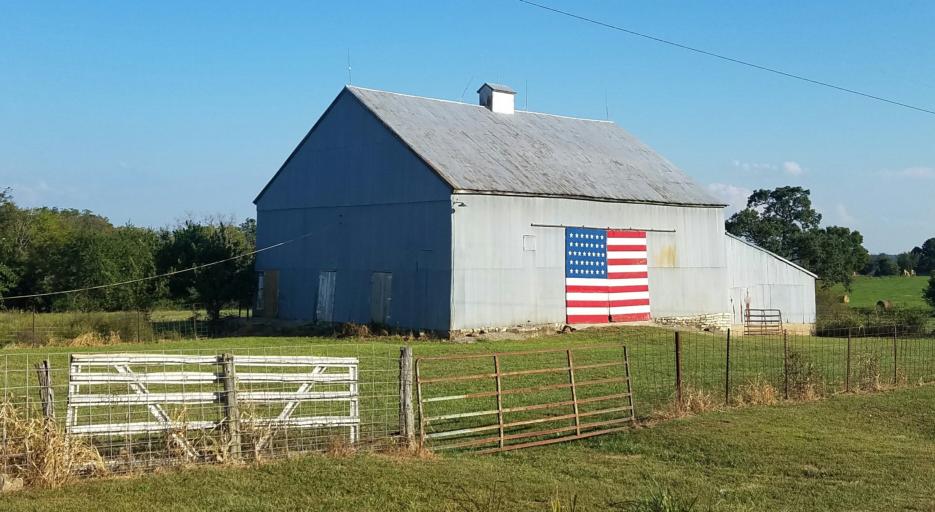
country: US
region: Missouri
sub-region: Moniteau County
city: California
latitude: 38.6758
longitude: -92.5868
